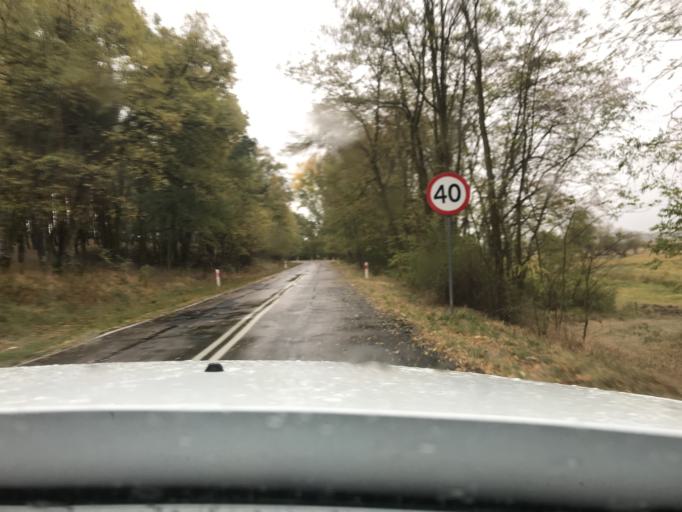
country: DE
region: Brandenburg
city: Neulewin
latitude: 52.7748
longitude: 14.3013
